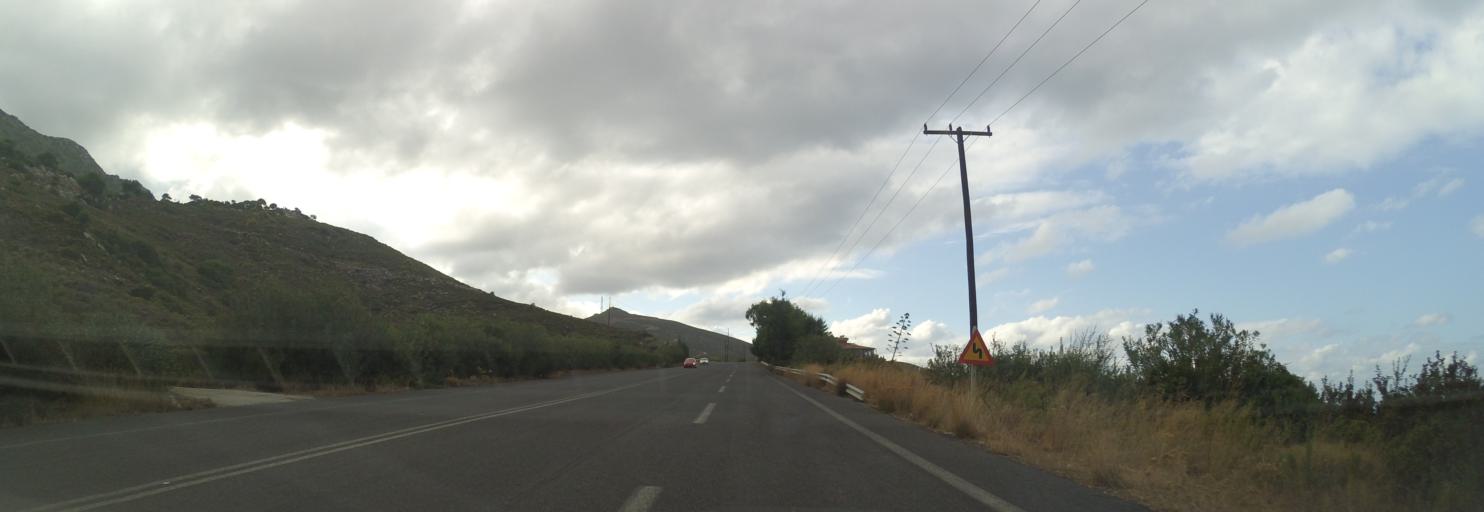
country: GR
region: Crete
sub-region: Nomos Rethymnis
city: Perama
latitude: 35.4094
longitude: 24.7723
